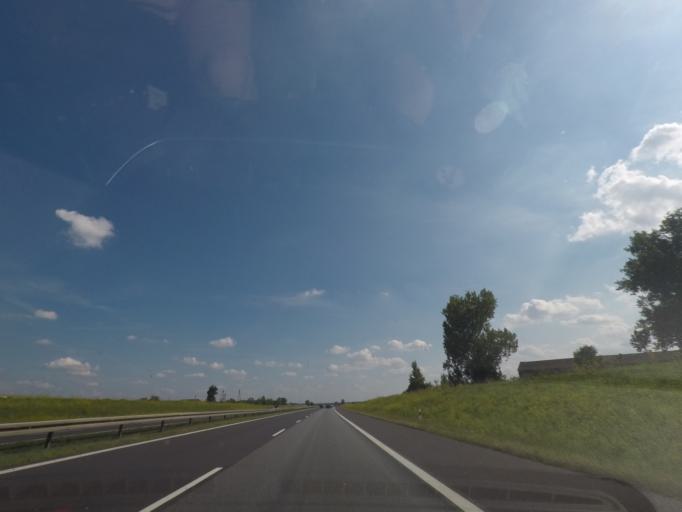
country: PL
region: Lodz Voivodeship
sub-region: Powiat piotrkowski
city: Moszczenica
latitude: 51.4686
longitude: 19.6330
